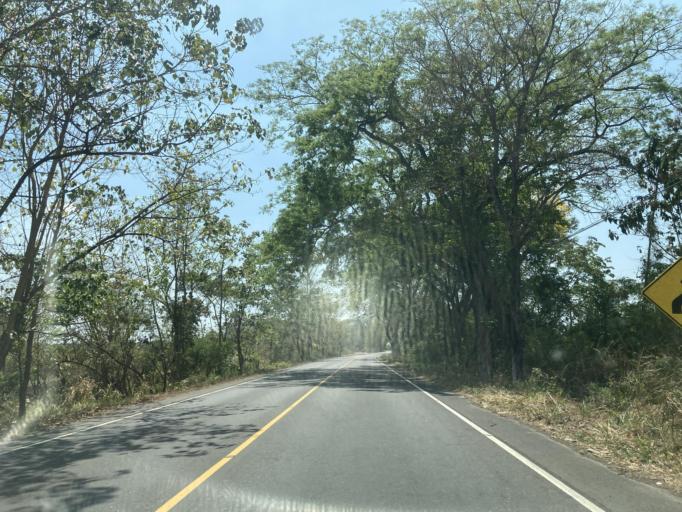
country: GT
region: Escuintla
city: Guanagazapa
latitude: 14.1869
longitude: -90.6927
